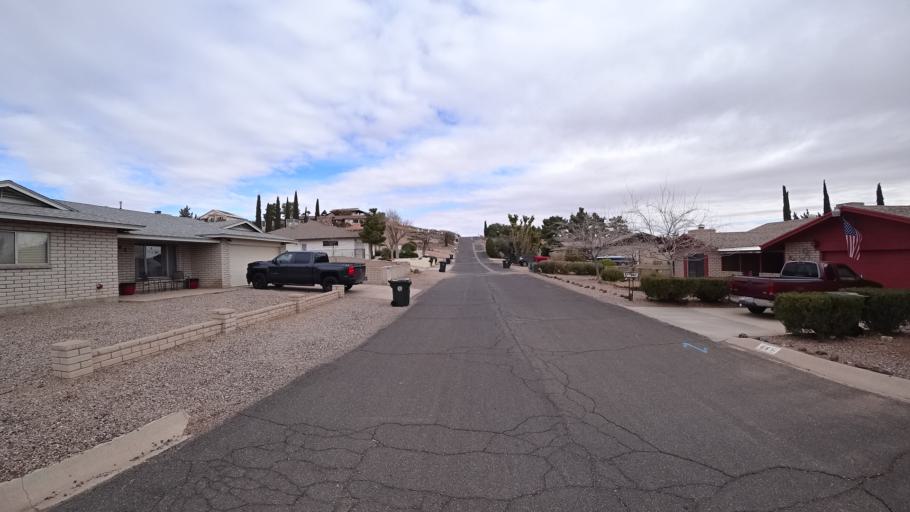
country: US
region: Arizona
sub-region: Mohave County
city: New Kingman-Butler
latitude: 35.2386
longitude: -114.0453
